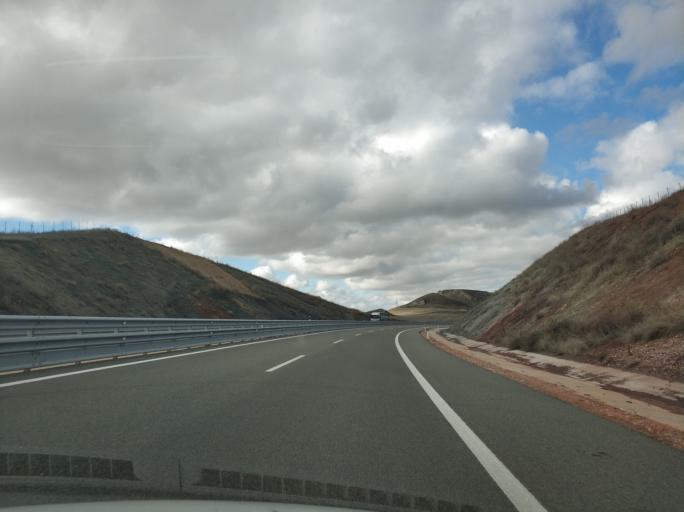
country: ES
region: Castille and Leon
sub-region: Provincia de Soria
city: Medinaceli
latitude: 41.1945
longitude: -2.4543
